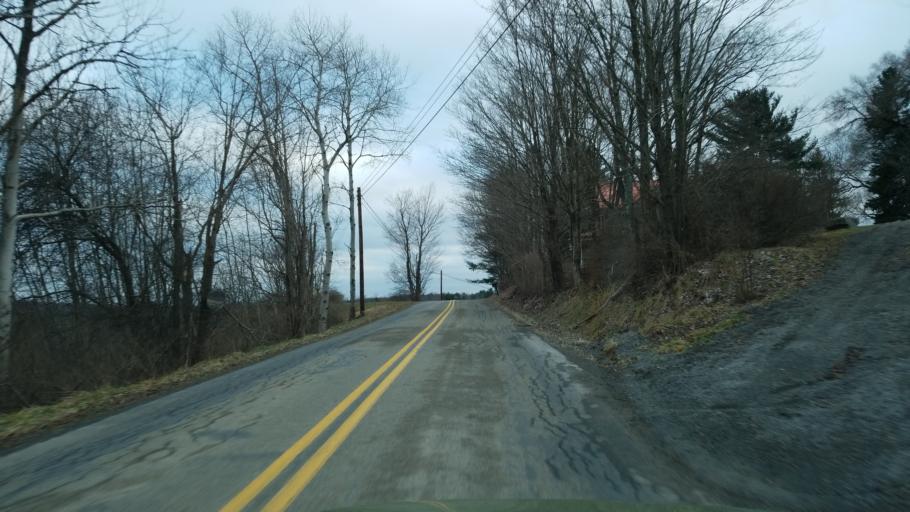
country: US
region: Pennsylvania
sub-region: Jefferson County
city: Falls Creek
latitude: 41.1770
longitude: -78.8136
